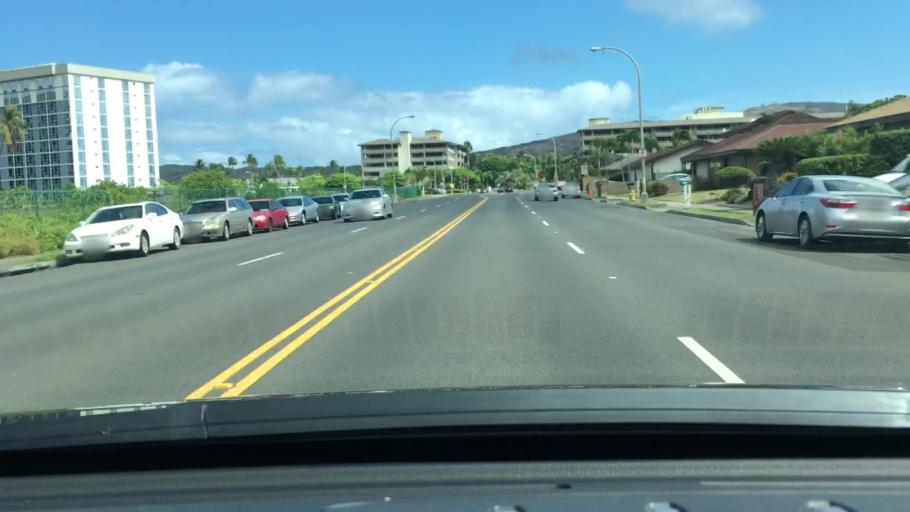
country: US
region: Hawaii
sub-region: Honolulu County
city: Waimanalo Beach
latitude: 21.2887
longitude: -157.7068
